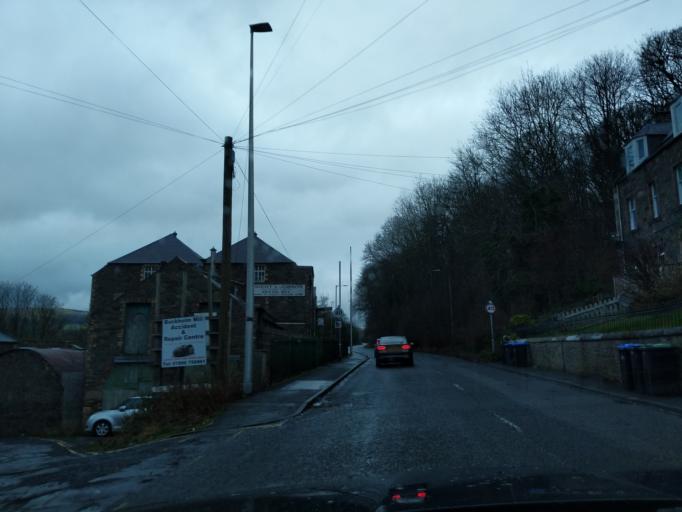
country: GB
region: Scotland
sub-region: The Scottish Borders
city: Galashiels
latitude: 55.6252
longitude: -2.8228
